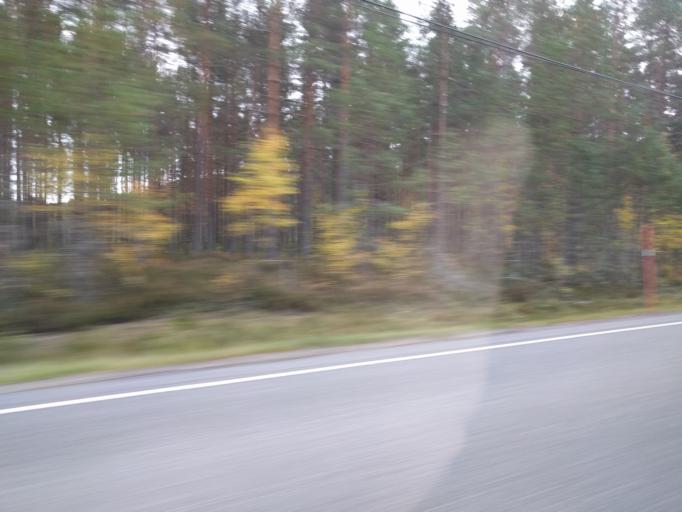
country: NO
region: Aust-Agder
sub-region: Evje og Hornnes
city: Evje
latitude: 58.4974
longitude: 7.7762
